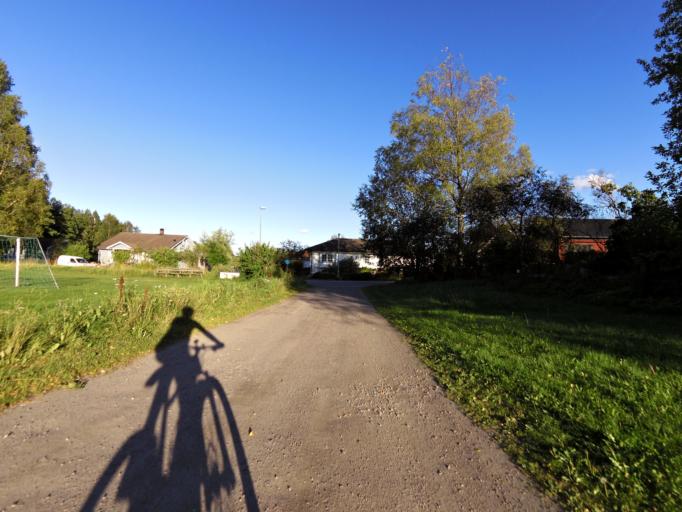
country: SE
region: Gaevleborg
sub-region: Gavle Kommun
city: Gavle
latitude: 60.7155
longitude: 17.1432
